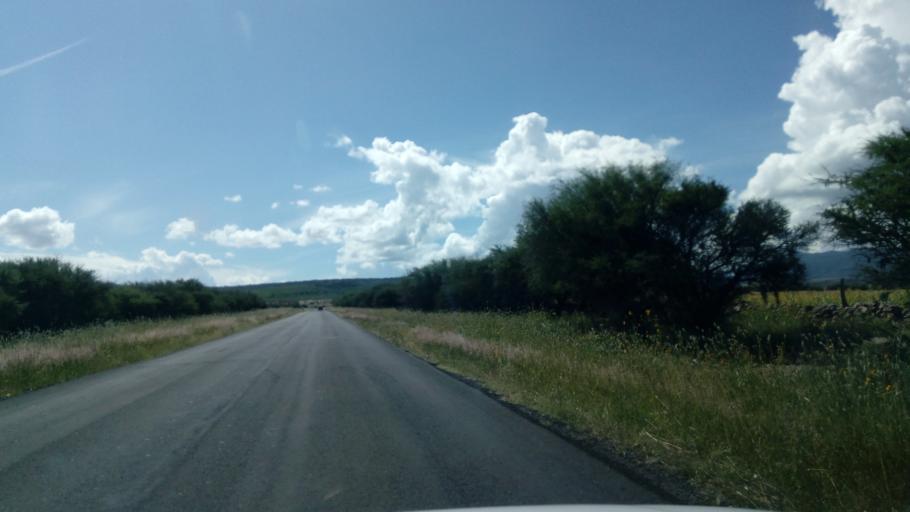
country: MX
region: Durango
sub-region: Durango
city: Jose Refugio Salcido
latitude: 23.8571
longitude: -104.4742
